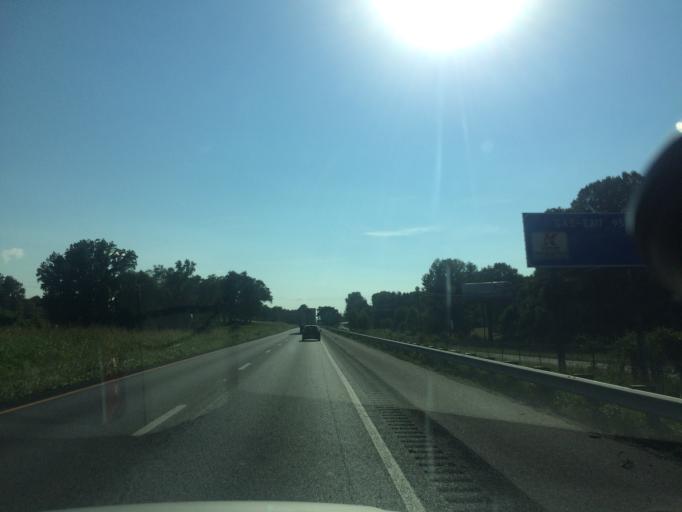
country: US
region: South Carolina
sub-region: Cherokee County
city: East Gaffney
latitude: 35.1049
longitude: -81.6182
